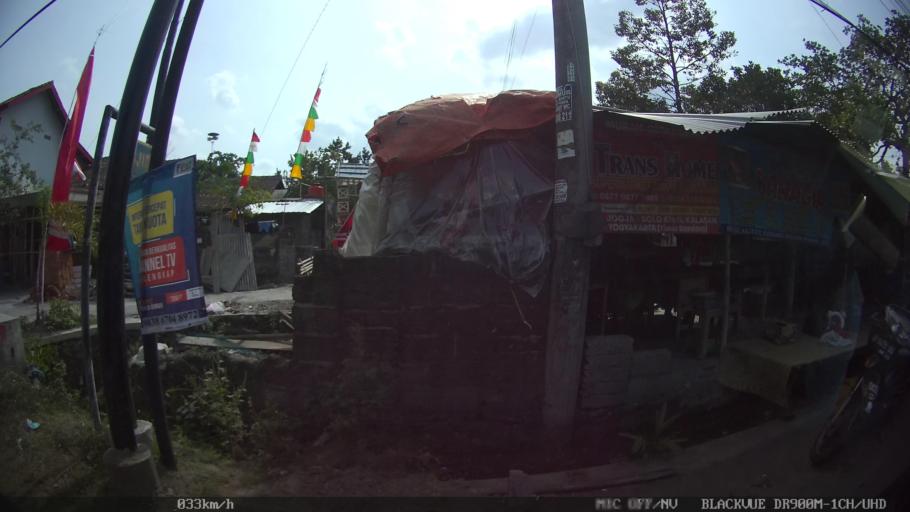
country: ID
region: Daerah Istimewa Yogyakarta
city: Depok
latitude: -7.7896
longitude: 110.4472
